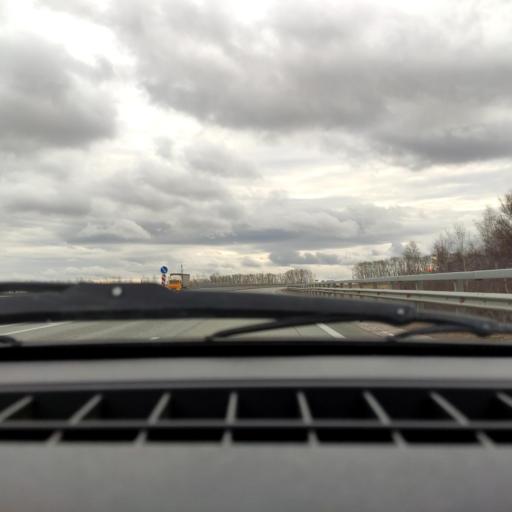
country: RU
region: Bashkortostan
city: Asanovo
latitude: 54.9645
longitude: 55.5829
